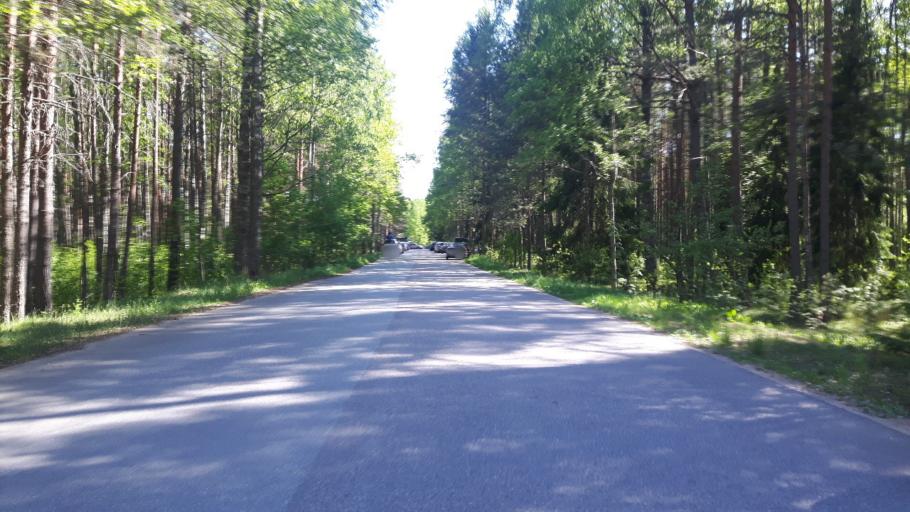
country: RU
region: Leningrad
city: Sista-Palkino
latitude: 59.7662
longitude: 28.7395
